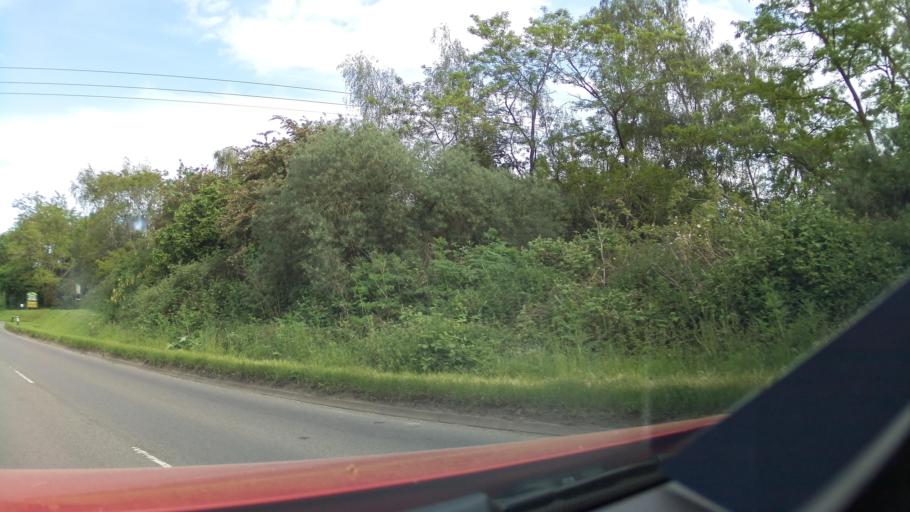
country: GB
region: England
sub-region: Worcestershire
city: Badsey
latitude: 52.0924
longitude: -1.9175
